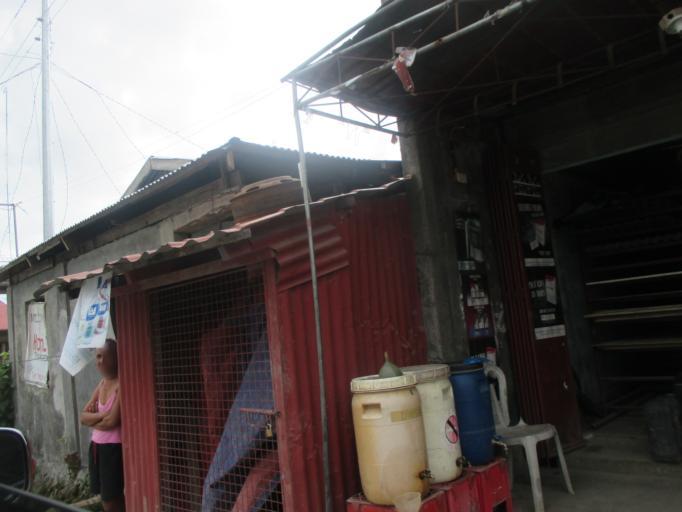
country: PH
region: Eastern Visayas
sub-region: Province of Eastern Samar
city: Lawa-an
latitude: 11.1071
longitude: 125.2123
